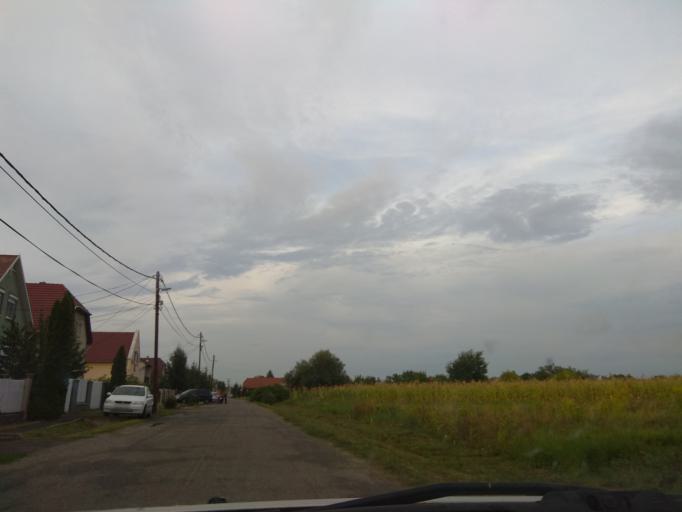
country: HU
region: Borsod-Abauj-Zemplen
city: Miskolc
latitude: 48.0724
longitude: 20.8231
